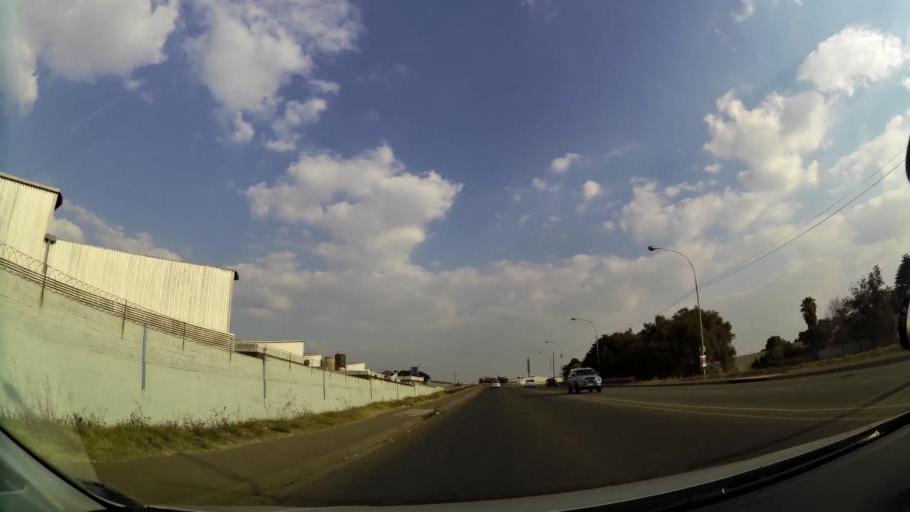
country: ZA
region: Gauteng
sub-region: City of Johannesburg Metropolitan Municipality
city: Modderfontein
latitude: -26.1171
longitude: 28.2082
